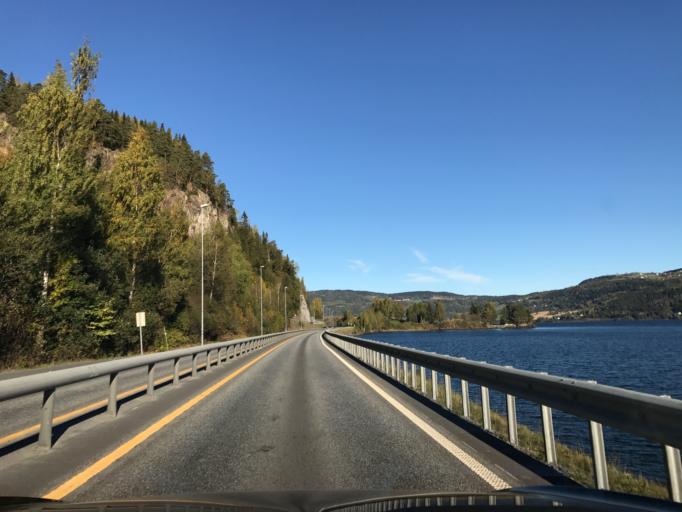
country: NO
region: Hedmark
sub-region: Ringsaker
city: Moelv
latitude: 60.9436
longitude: 10.6423
